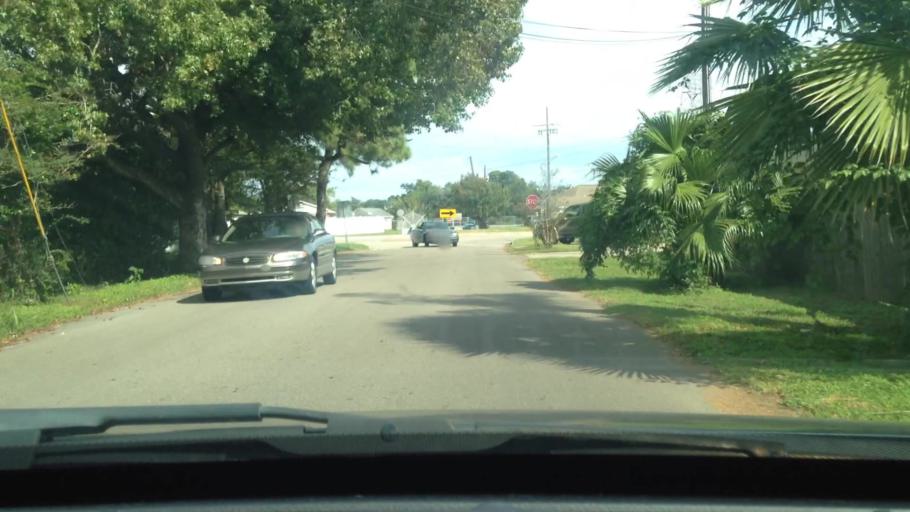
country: US
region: Louisiana
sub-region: Jefferson Parish
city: River Ridge
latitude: 29.9845
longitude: -90.2164
